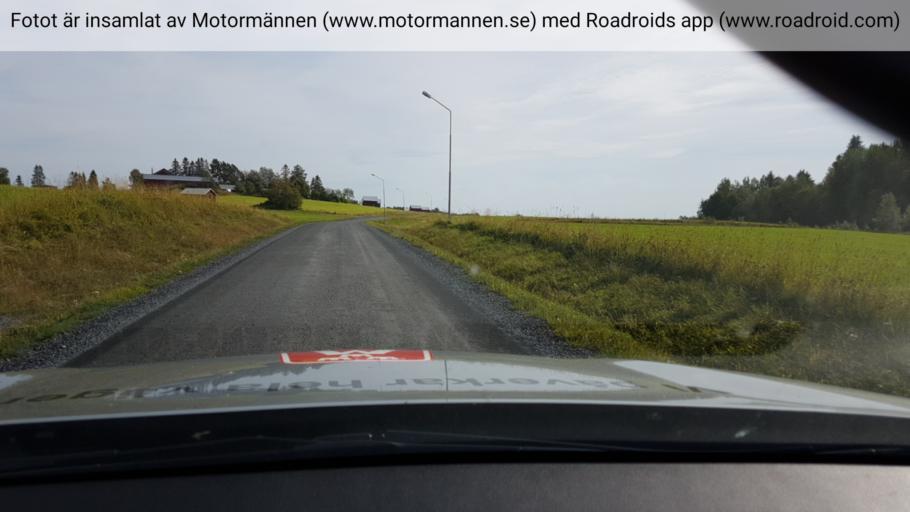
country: SE
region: Jaemtland
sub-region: Krokoms Kommun
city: Valla
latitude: 63.3645
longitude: 13.9587
